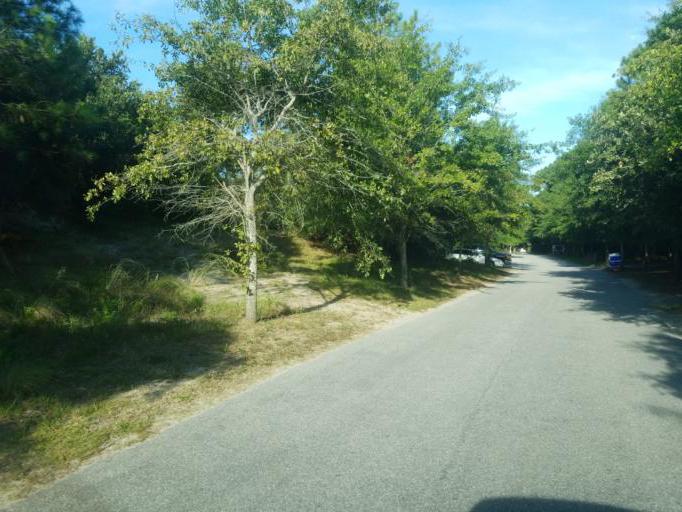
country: US
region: North Carolina
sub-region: Currituck County
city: Currituck
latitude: 36.3762
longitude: -75.8294
